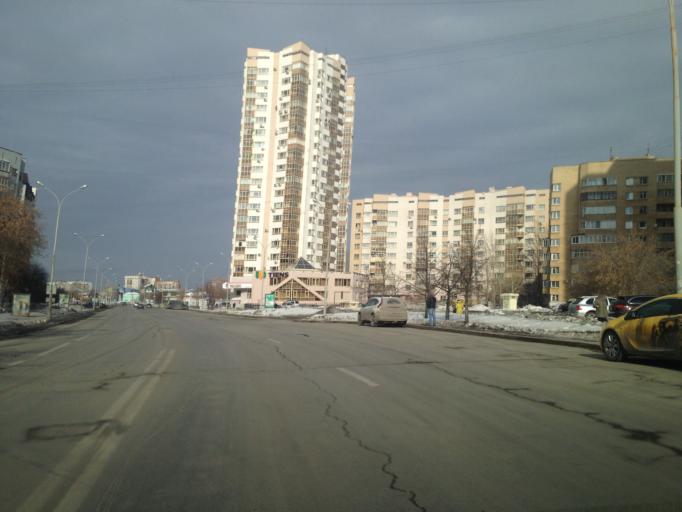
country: RU
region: Sverdlovsk
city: Yekaterinburg
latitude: 56.8393
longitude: 60.5897
